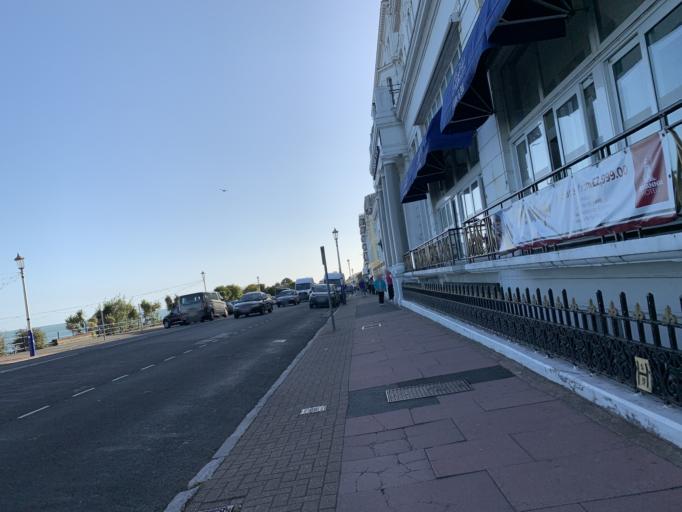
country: GB
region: England
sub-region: East Sussex
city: Eastbourne
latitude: 50.7645
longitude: 0.2888
